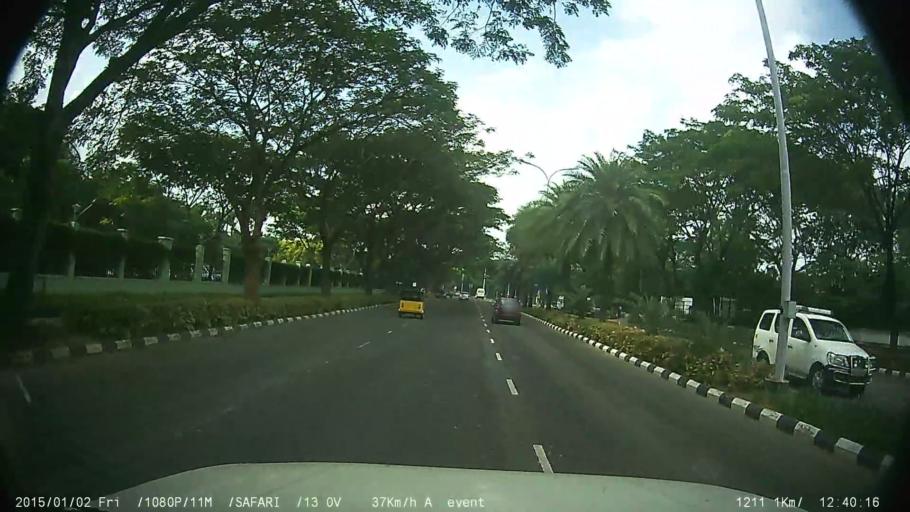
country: IN
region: Tamil Nadu
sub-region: Kancheepuram
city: Singapperumalkovil
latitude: 12.7351
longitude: 80.0091
